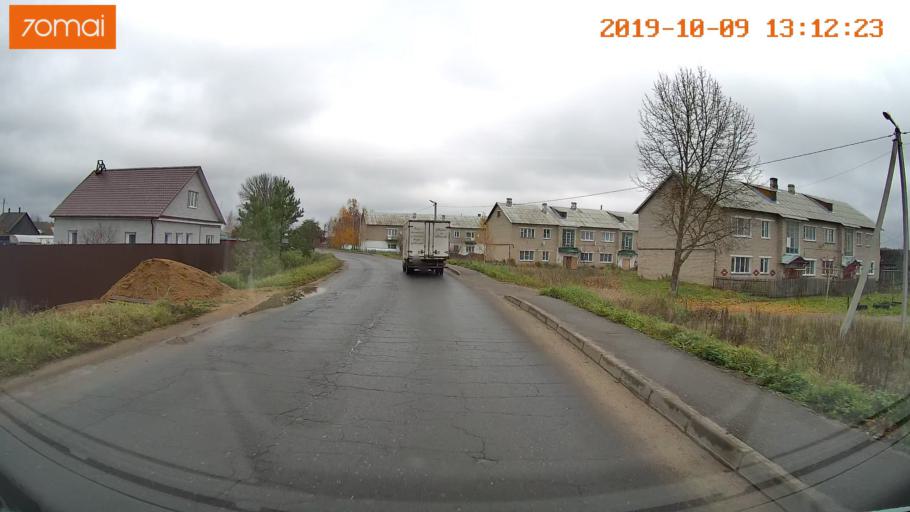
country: RU
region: Jaroslavl
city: Lyubim
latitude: 58.3606
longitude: 40.7024
